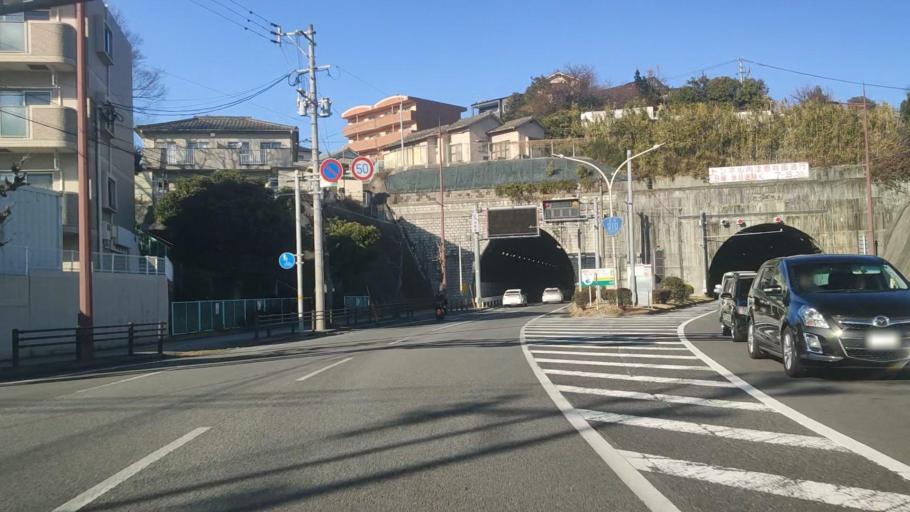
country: JP
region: Oita
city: Oita
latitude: 33.2189
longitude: 131.5948
